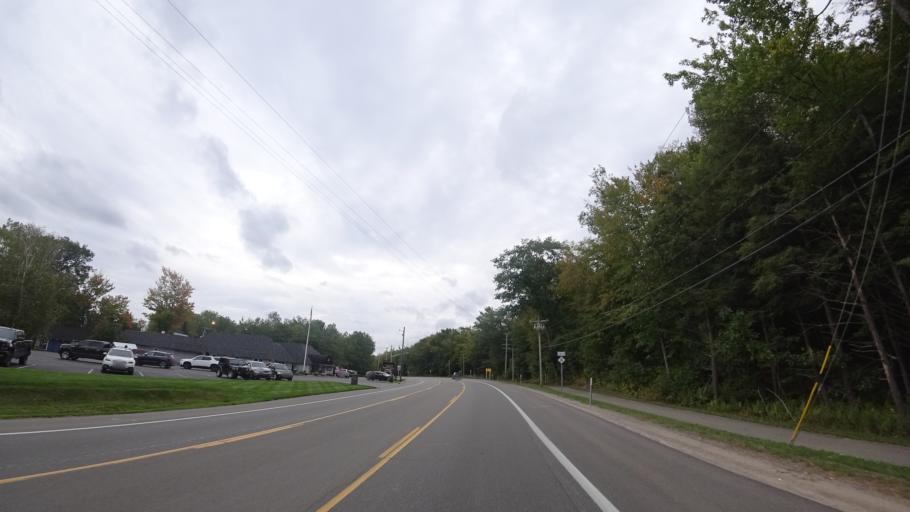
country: US
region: Michigan
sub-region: Emmet County
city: Petoskey
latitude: 45.4145
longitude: -84.9045
